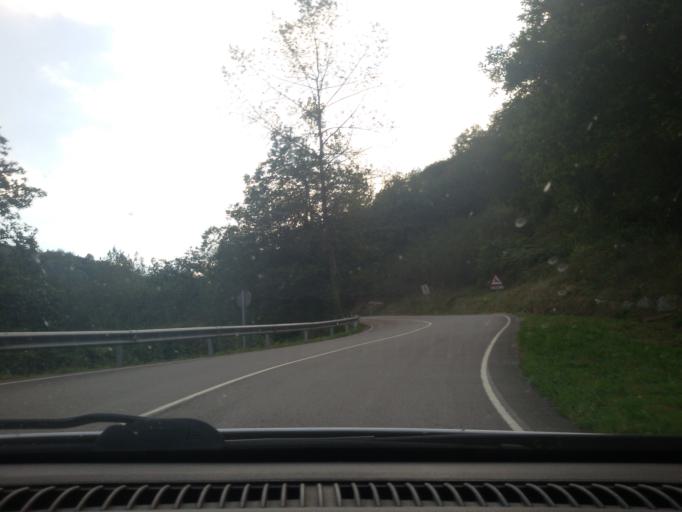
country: ES
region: Asturias
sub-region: Province of Asturias
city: Bimenes
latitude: 43.3379
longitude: -5.5775
